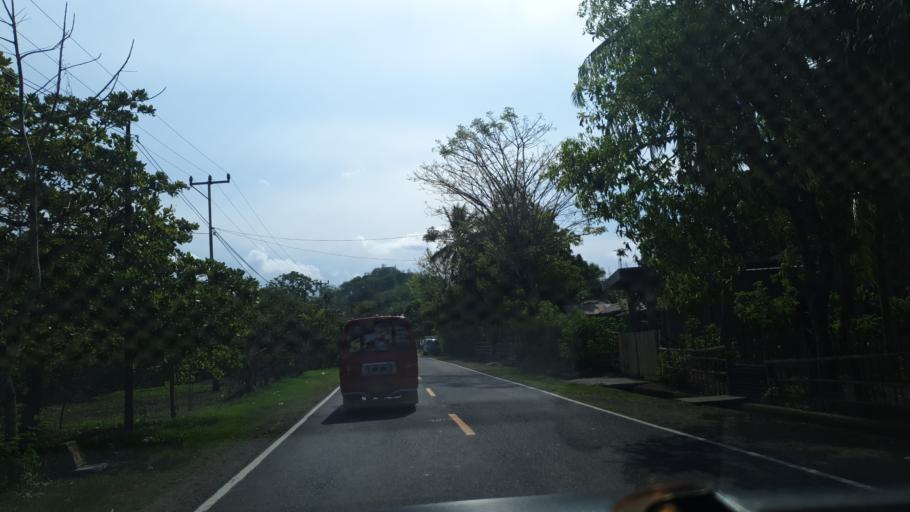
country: ID
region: East Nusa Tenggara
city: Nangalimang
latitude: -8.6545
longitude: 122.2047
